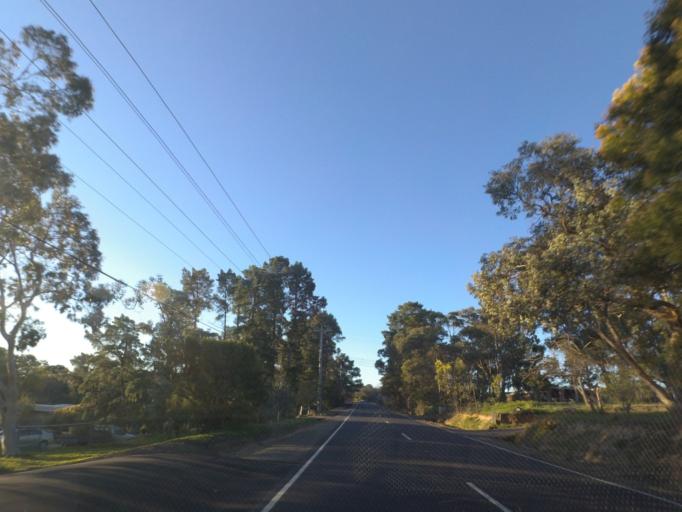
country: AU
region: Victoria
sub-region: Manningham
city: Park Orchards
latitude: -37.7641
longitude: 145.2188
